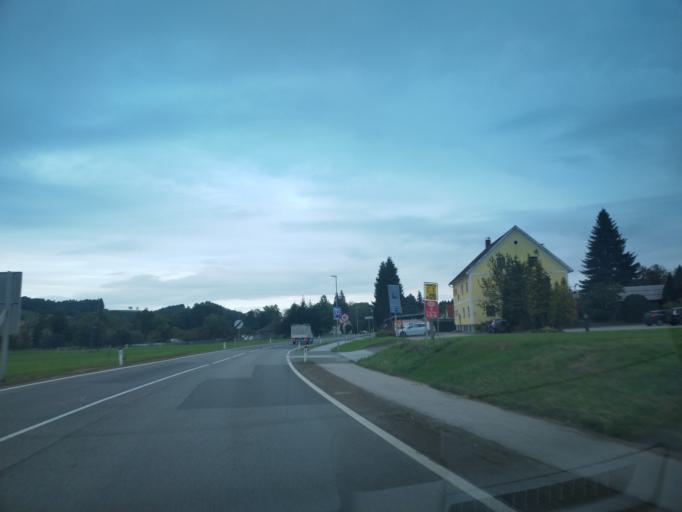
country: AT
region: Styria
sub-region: Politischer Bezirk Deutschlandsberg
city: Aibl
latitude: 46.6821
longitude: 15.2308
